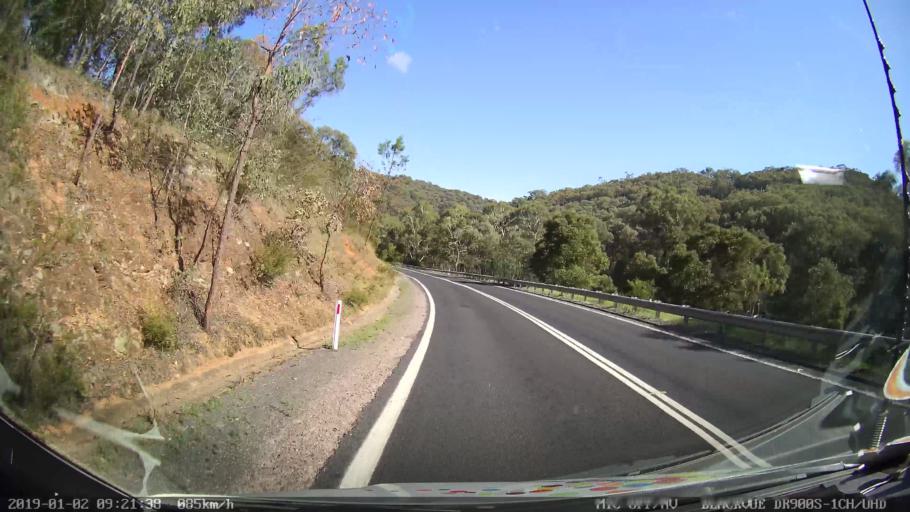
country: AU
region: New South Wales
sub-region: Tumut Shire
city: Tumut
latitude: -35.4034
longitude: 148.2914
